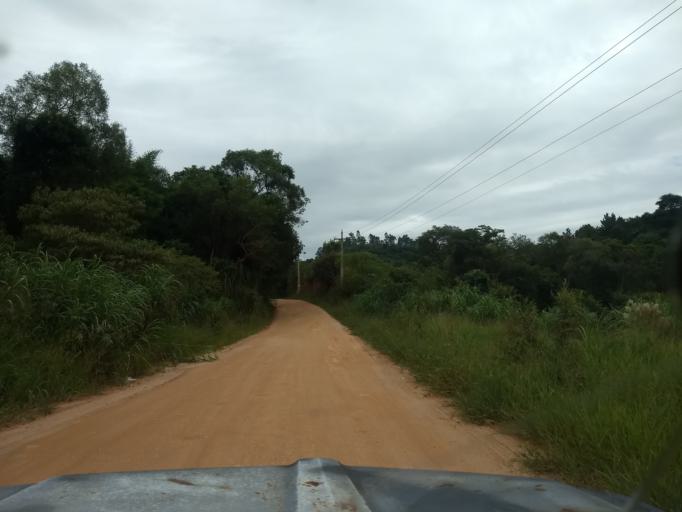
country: BR
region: Sao Paulo
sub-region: Cabreuva
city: Cabreuva
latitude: -23.4135
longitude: -47.1974
